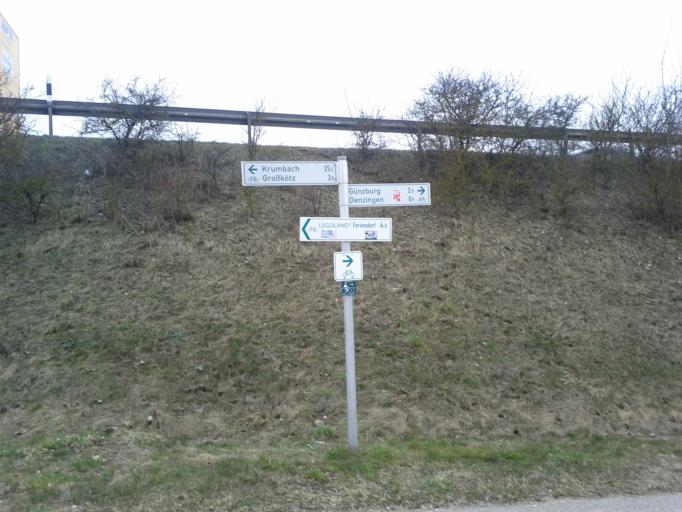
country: DE
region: Bavaria
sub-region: Swabia
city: Guenzburg
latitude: 48.4411
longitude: 10.2890
